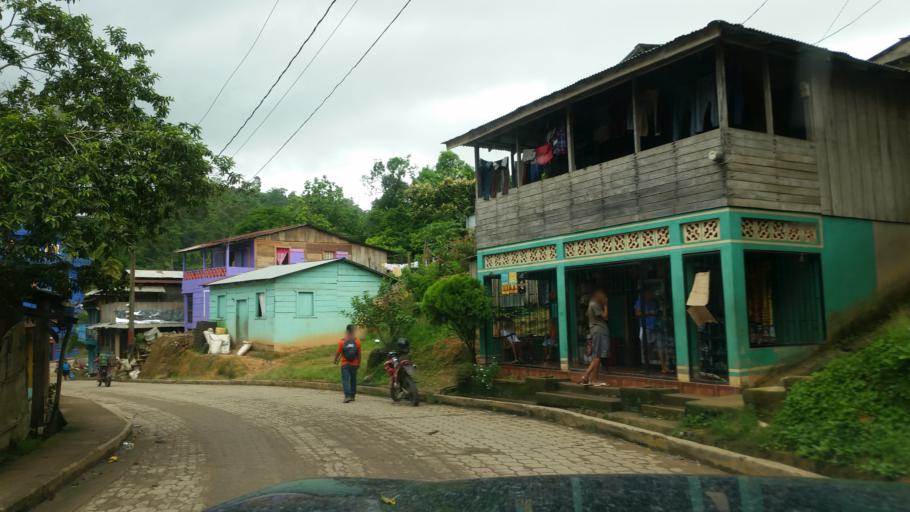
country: NI
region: Atlantico Norte (RAAN)
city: Bonanza
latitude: 14.0311
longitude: -84.6008
